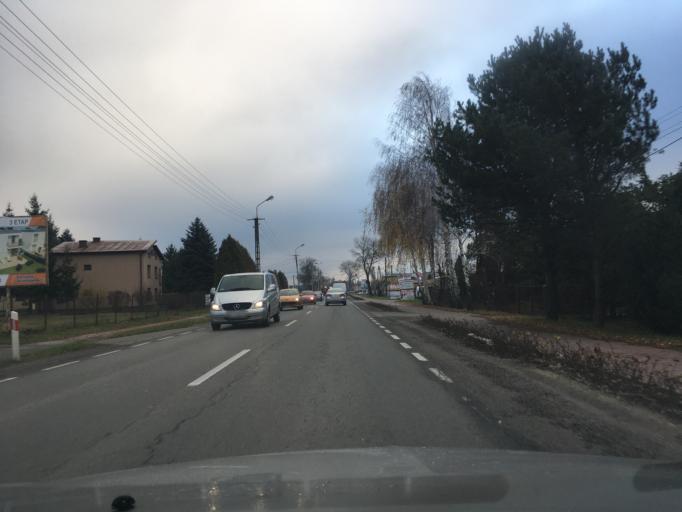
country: PL
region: Masovian Voivodeship
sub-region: Powiat piaseczynski
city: Lesznowola
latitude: 52.0840
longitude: 20.9568
